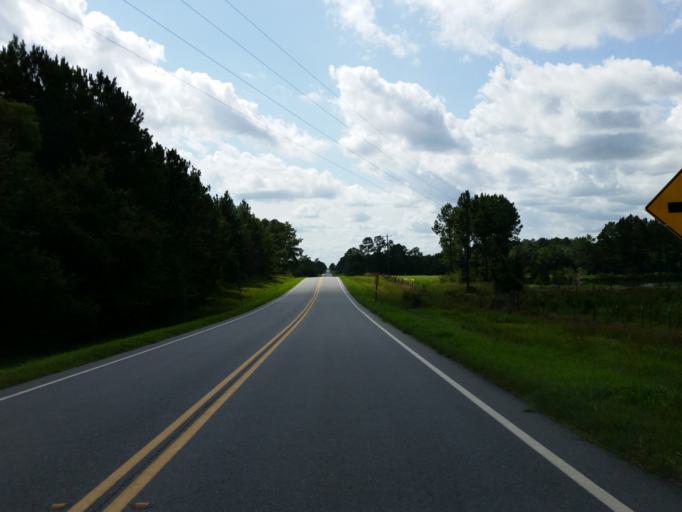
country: US
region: Georgia
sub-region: Turner County
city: Ashburn
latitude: 31.6446
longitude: -83.5338
